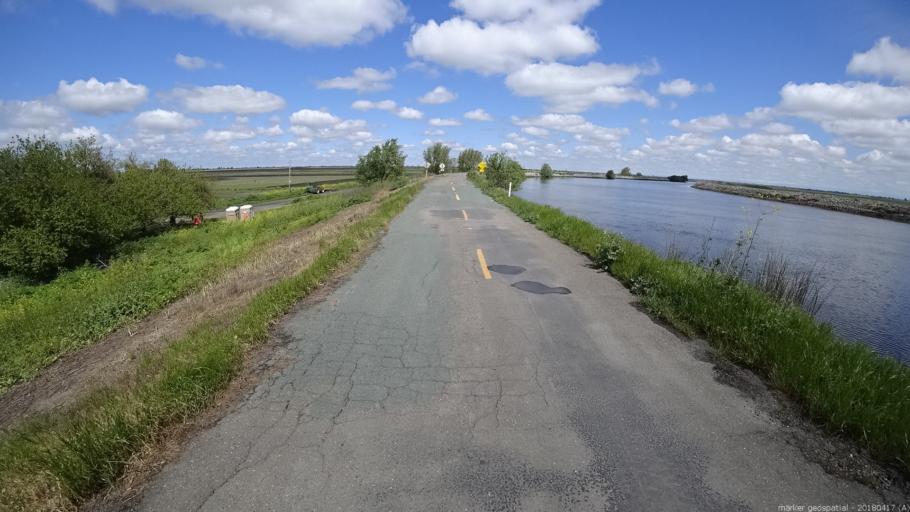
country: US
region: California
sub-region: Sacramento County
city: Walnut Grove
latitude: 38.1676
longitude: -121.5308
